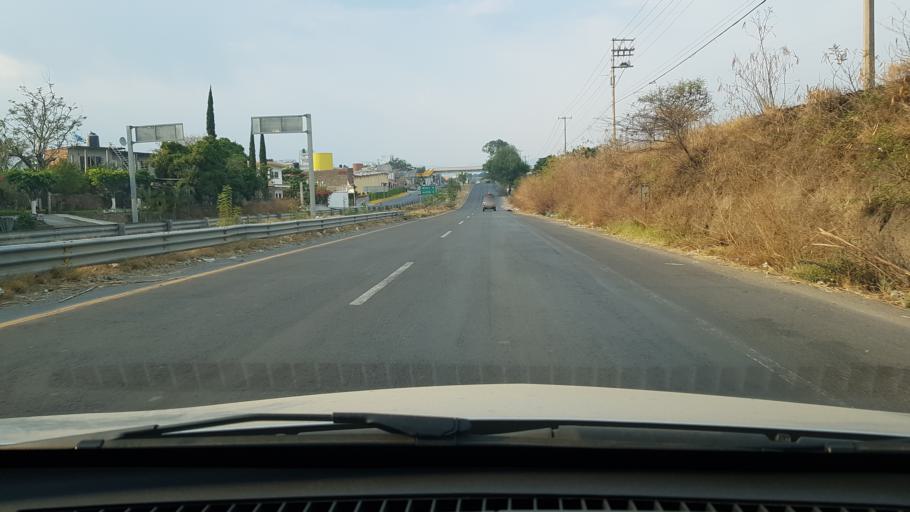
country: MX
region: Morelos
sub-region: Yecapixtla
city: Juan Morales
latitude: 18.8005
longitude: -98.9156
